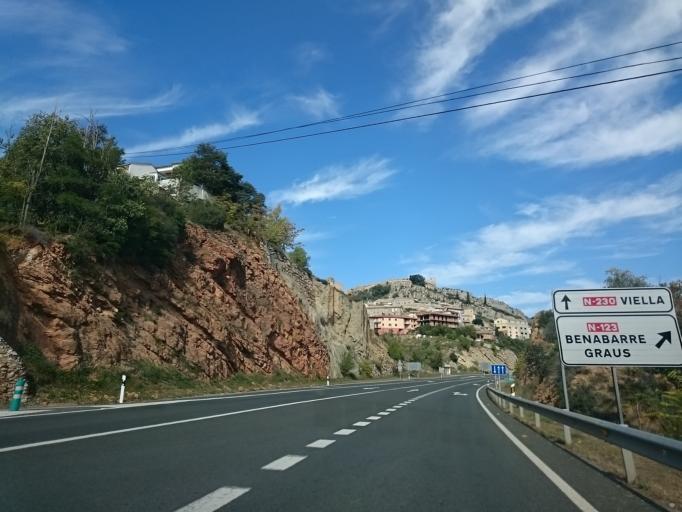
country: ES
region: Aragon
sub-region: Provincia de Huesca
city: Benavarri / Benabarre
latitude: 42.1028
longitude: 0.4846
